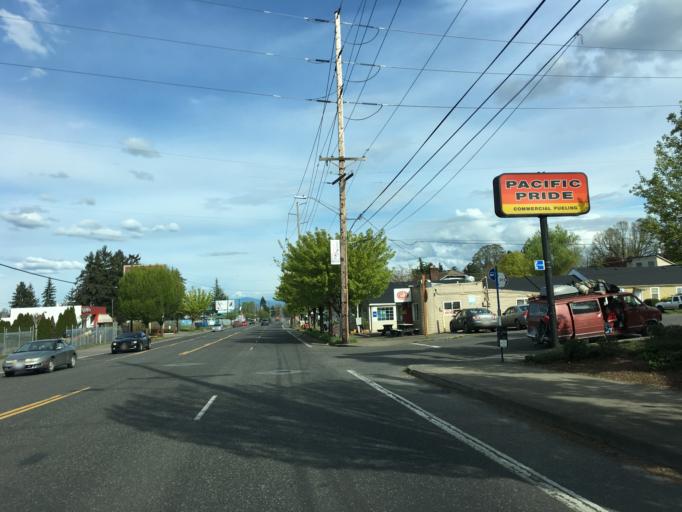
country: US
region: Oregon
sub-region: Multnomah County
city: Lents
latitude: 45.5579
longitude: -122.5447
